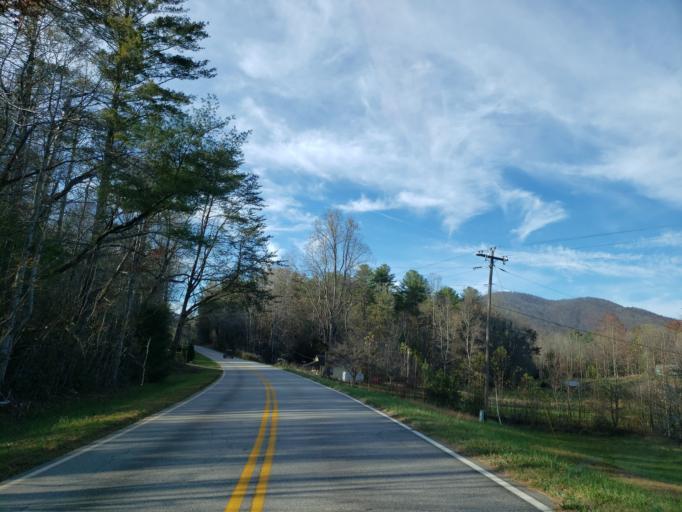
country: US
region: Georgia
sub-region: Lumpkin County
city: Dahlonega
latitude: 34.6236
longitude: -84.0858
